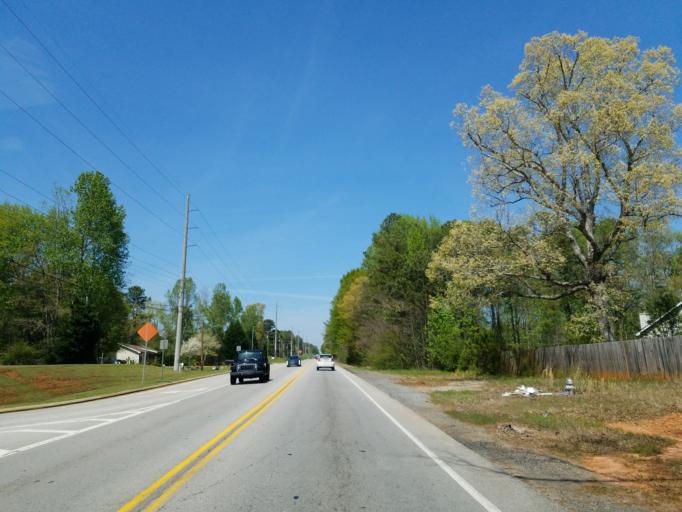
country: US
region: Georgia
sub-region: Paulding County
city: Dallas
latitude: 33.8771
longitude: -84.8406
